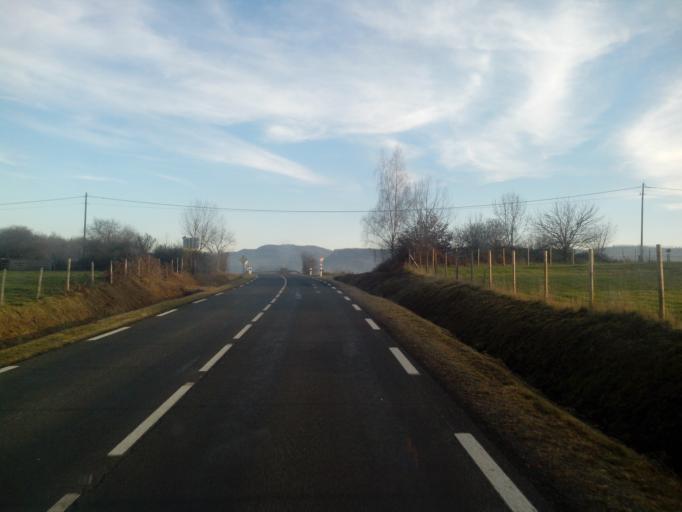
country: FR
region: Auvergne
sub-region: Departement du Cantal
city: Ydes
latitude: 45.3595
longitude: 2.4723
